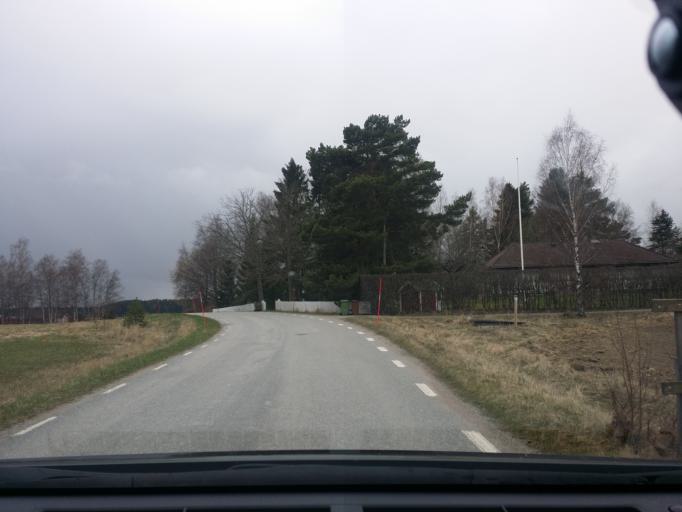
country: SE
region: Uppsala
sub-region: Enkopings Kommun
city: Enkoping
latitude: 59.6792
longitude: 17.0368
